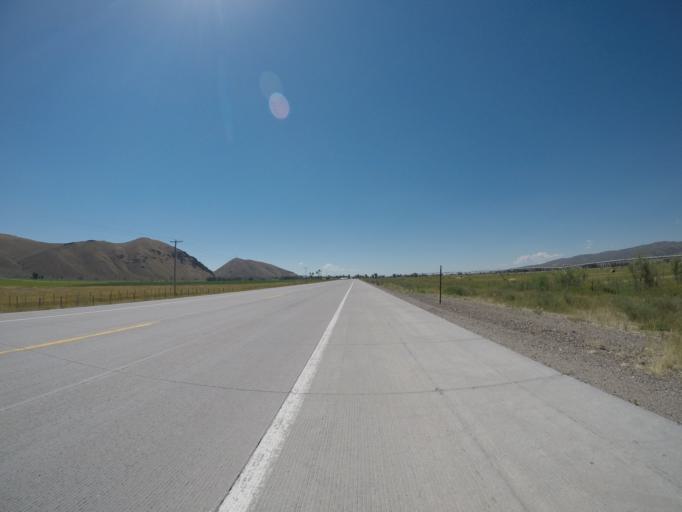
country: US
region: Idaho
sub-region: Bear Lake County
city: Montpelier
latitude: 42.1087
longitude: -110.9554
